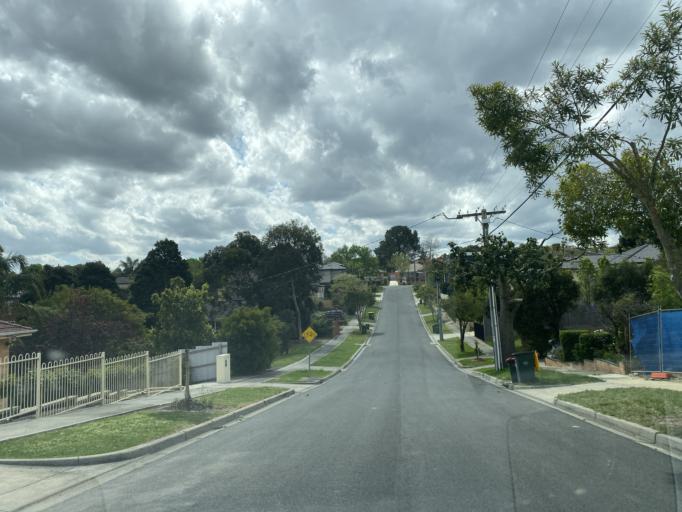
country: AU
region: Victoria
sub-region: Whitehorse
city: Burwood
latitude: -37.8558
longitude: 145.1242
